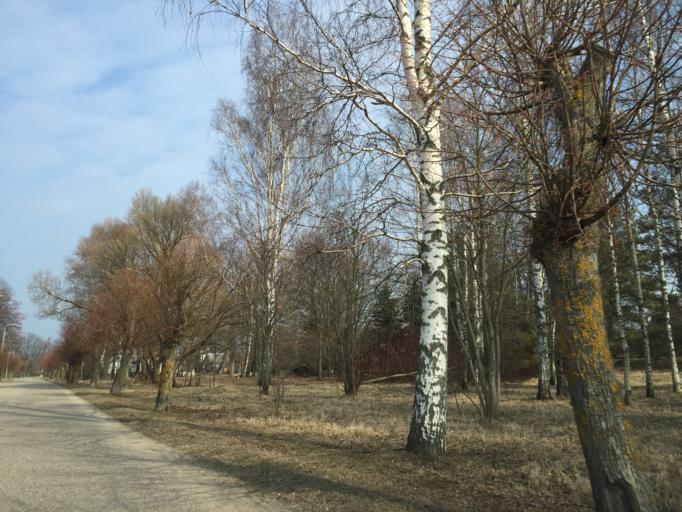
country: LV
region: Salacgrivas
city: Ainazi
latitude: 57.8685
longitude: 24.3602
